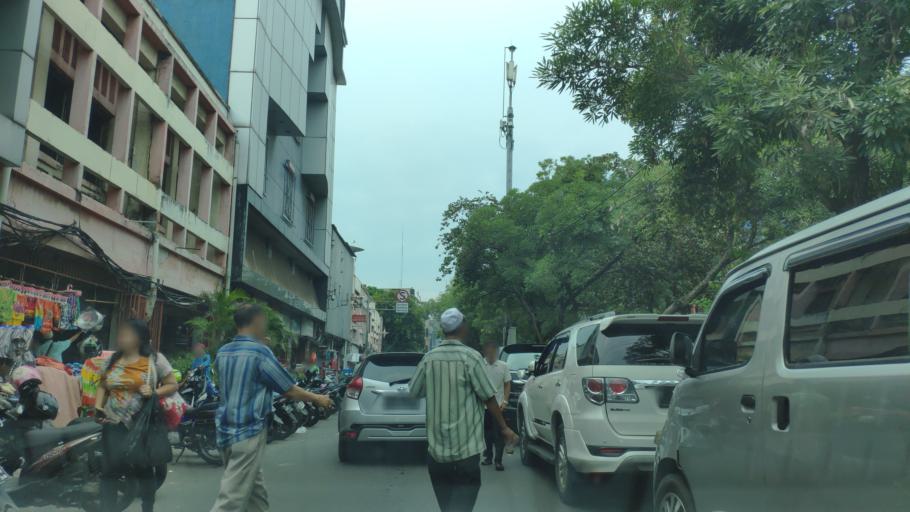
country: ID
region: Jakarta Raya
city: Jakarta
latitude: -6.1416
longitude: 106.8131
